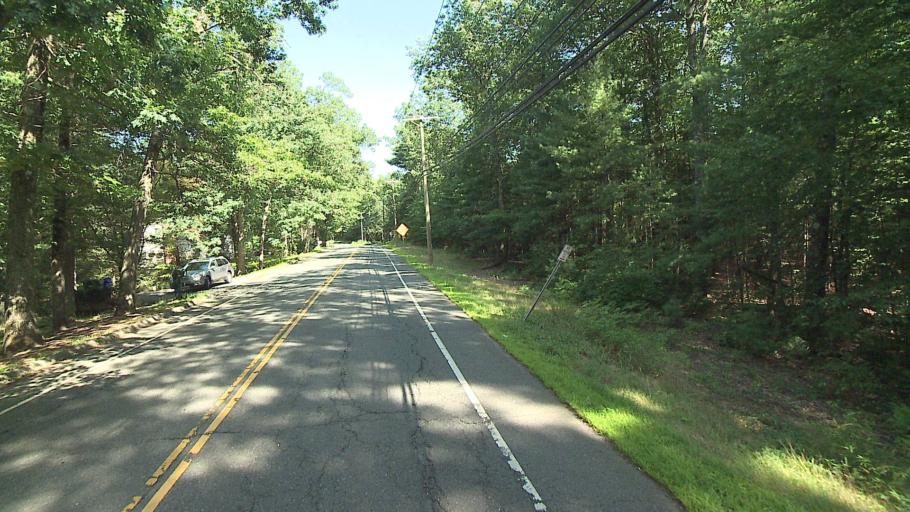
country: US
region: Connecticut
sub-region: Hartford County
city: West Simsbury
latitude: 41.8685
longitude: -72.8373
